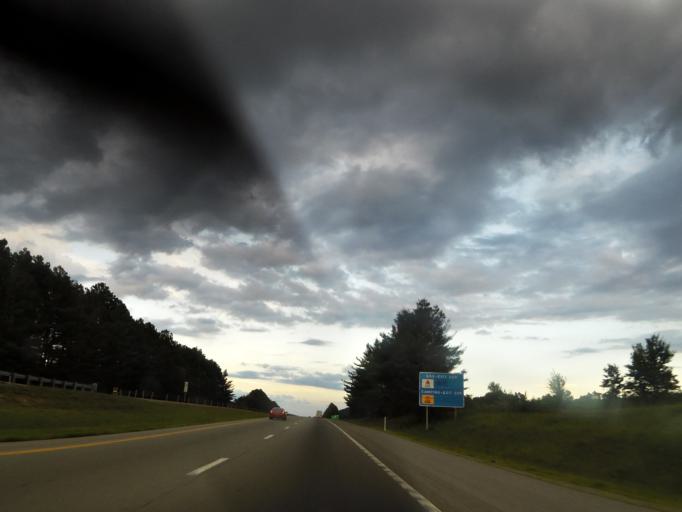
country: US
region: Tennessee
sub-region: Cumberland County
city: Fairfield Glade
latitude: 35.9154
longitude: -84.9016
